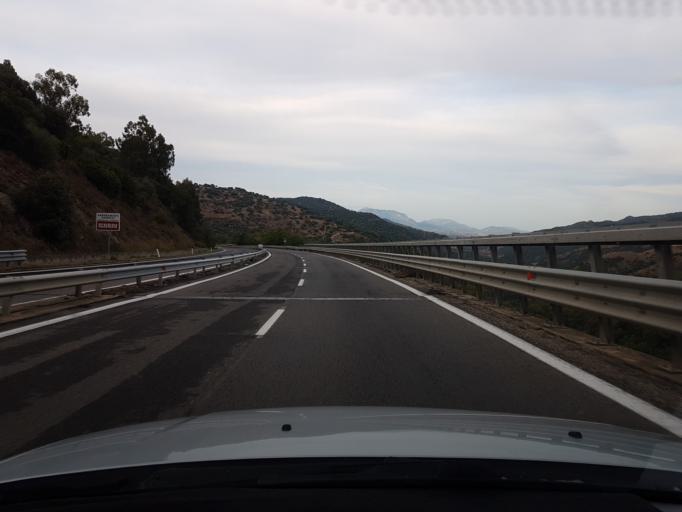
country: IT
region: Sardinia
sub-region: Provincia di Nuoro
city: Nuoro
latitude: 40.3348
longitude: 9.2981
